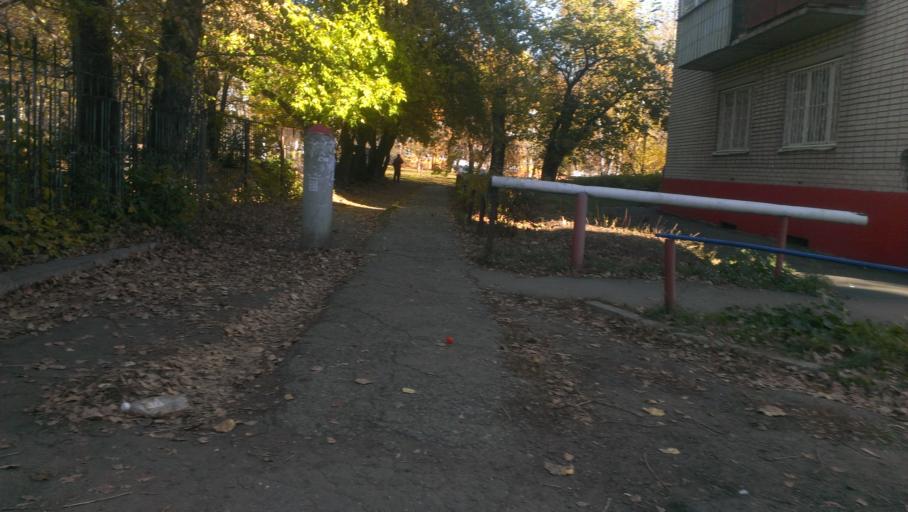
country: RU
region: Altai Krai
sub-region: Gorod Barnaulskiy
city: Barnaul
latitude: 53.3653
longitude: 83.6848
